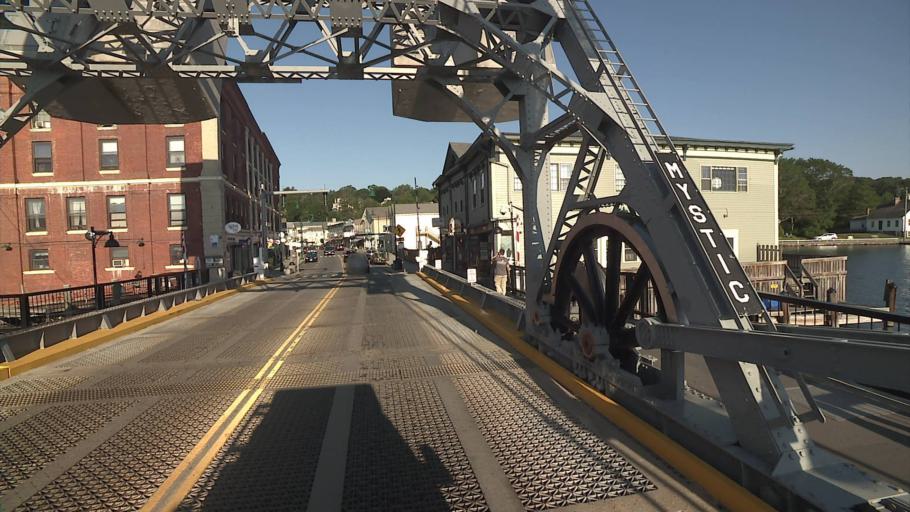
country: US
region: Connecticut
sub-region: New London County
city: Mystic
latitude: 41.3548
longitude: -71.9688
